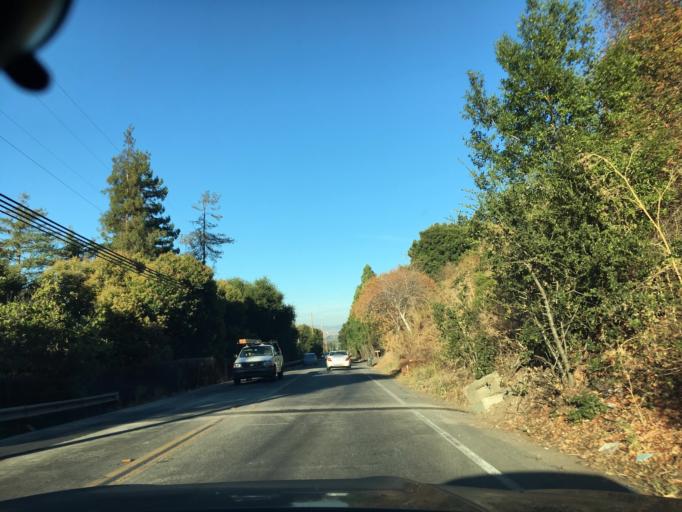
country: US
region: California
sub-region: Santa Clara County
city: Cambrian Park
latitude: 37.2361
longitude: -121.9385
